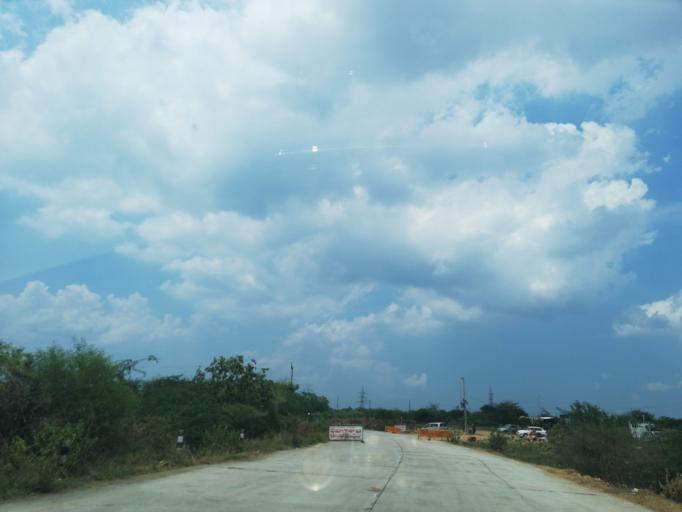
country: IN
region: Andhra Pradesh
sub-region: Guntur
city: Macherla
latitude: 16.5677
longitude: 79.3334
